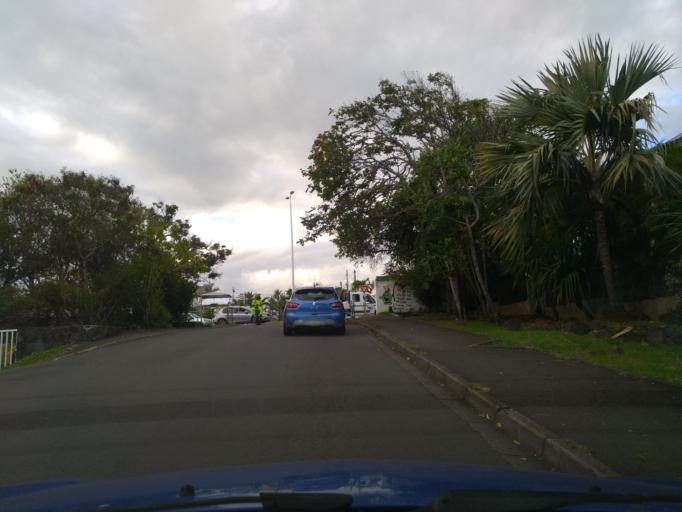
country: RE
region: Reunion
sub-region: Reunion
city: Saint-Pierre
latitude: -21.3311
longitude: 55.4748
